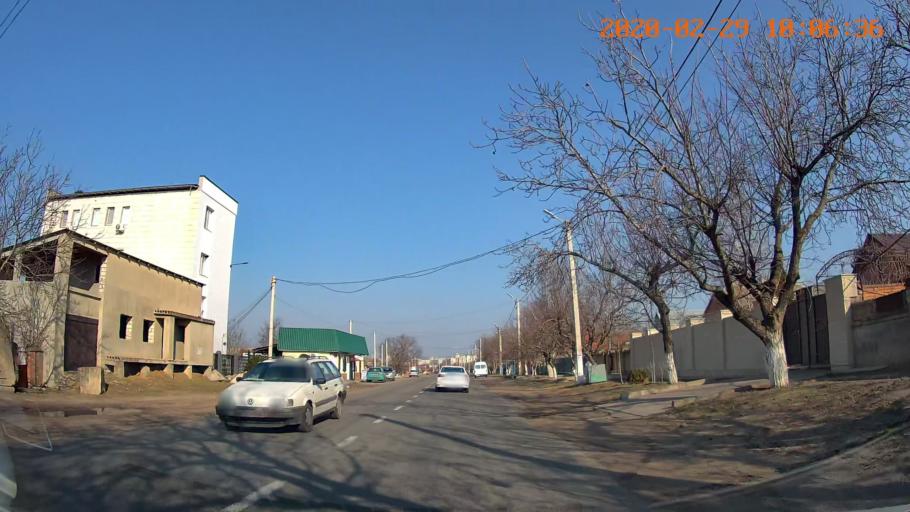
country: MD
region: Telenesti
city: Tiraspolul Nou
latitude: 46.8159
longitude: 29.6689
